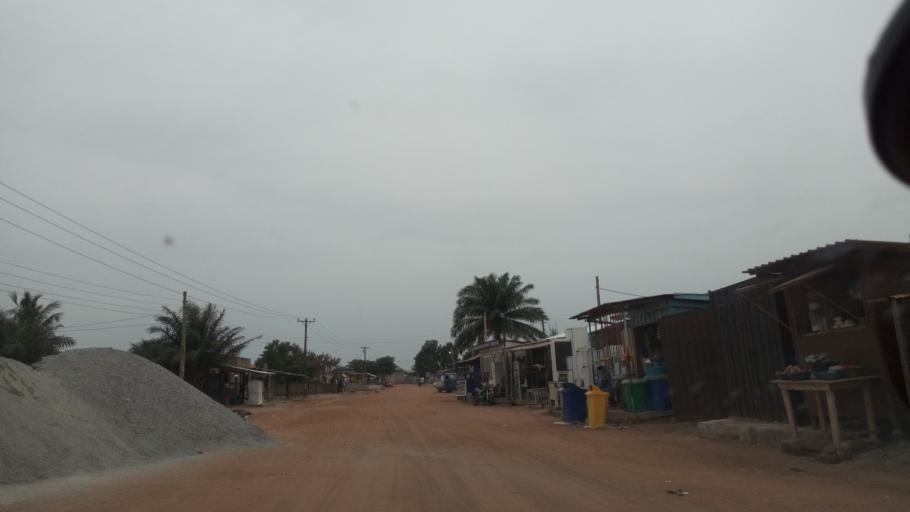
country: GH
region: Greater Accra
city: Medina Estates
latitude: 5.7049
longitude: -0.1338
